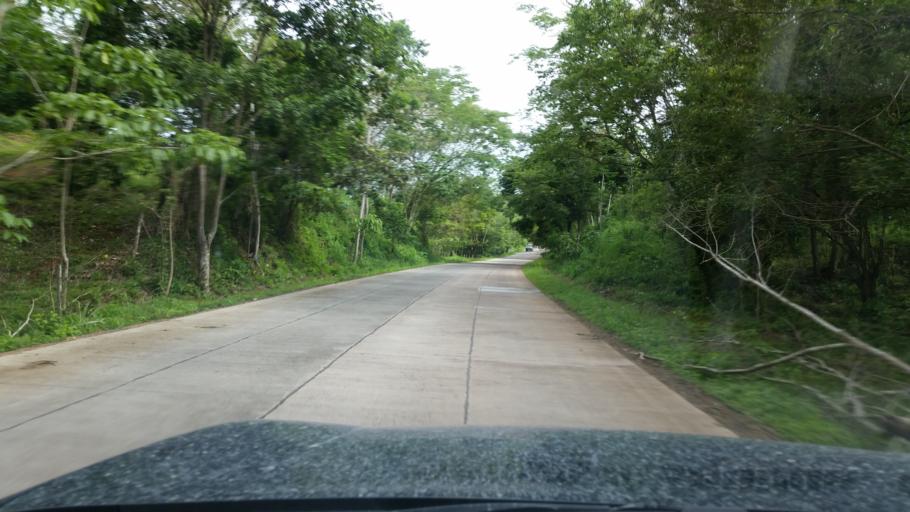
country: NI
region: Atlantico Norte (RAAN)
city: Siuna
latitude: 13.5571
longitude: -84.8183
